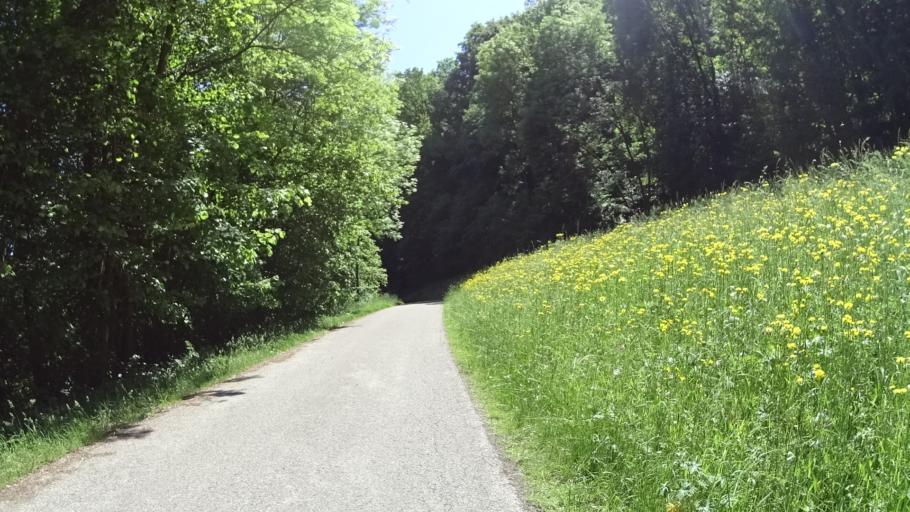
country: DE
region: Bavaria
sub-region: Regierungsbezirk Mittelfranken
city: Adelshofen
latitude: 49.4225
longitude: 10.1458
